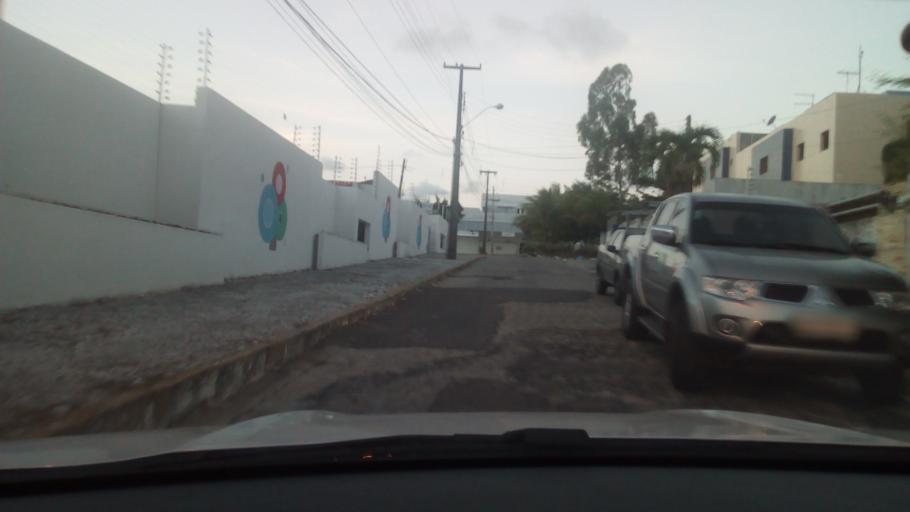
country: BR
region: Paraiba
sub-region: Joao Pessoa
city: Joao Pessoa
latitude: -7.1114
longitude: -34.8438
